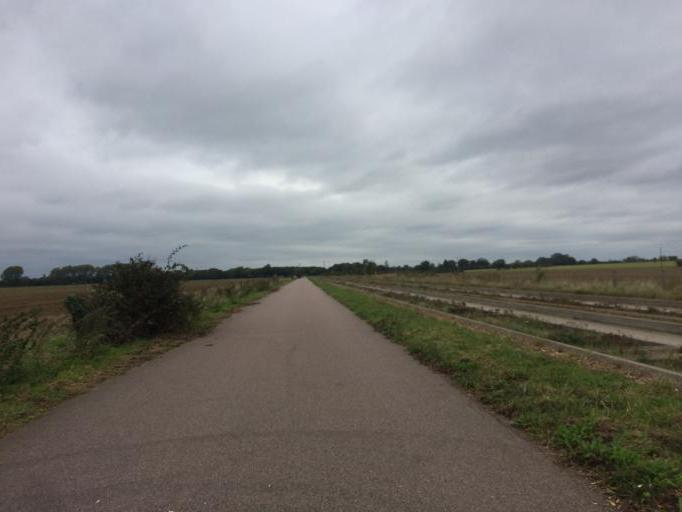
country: GB
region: England
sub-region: Cambridgeshire
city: Histon
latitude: 52.2559
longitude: 0.0888
